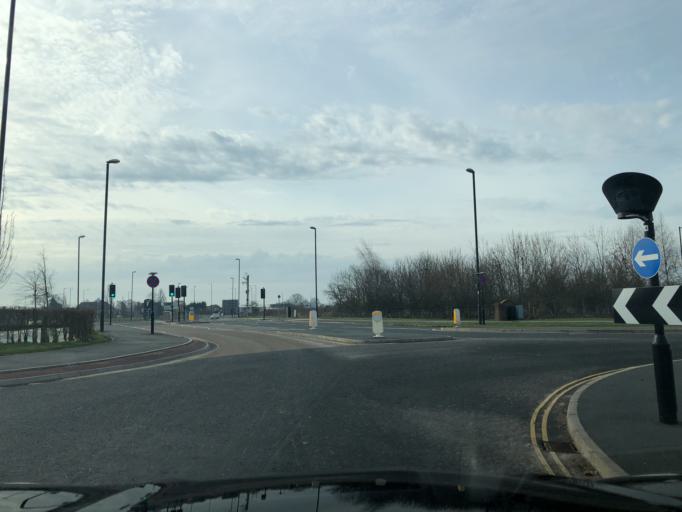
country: GB
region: England
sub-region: City of York
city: Huntington
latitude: 53.9822
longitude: -1.0504
